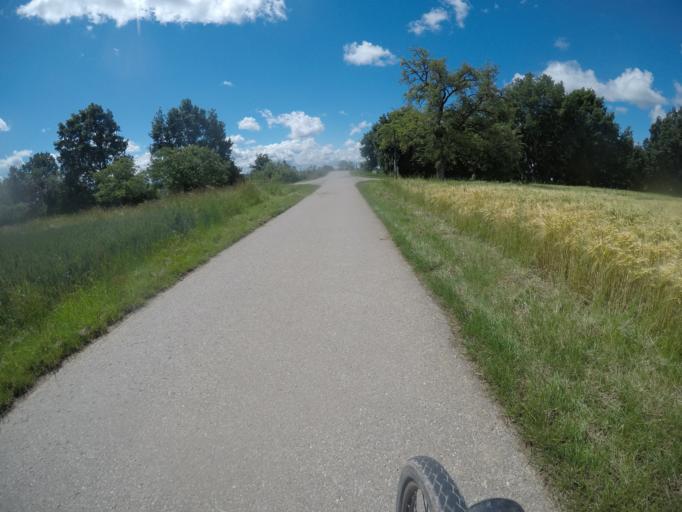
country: DE
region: Baden-Wuerttemberg
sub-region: Regierungsbezirk Stuttgart
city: Motzingen
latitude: 48.4856
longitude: 8.7497
